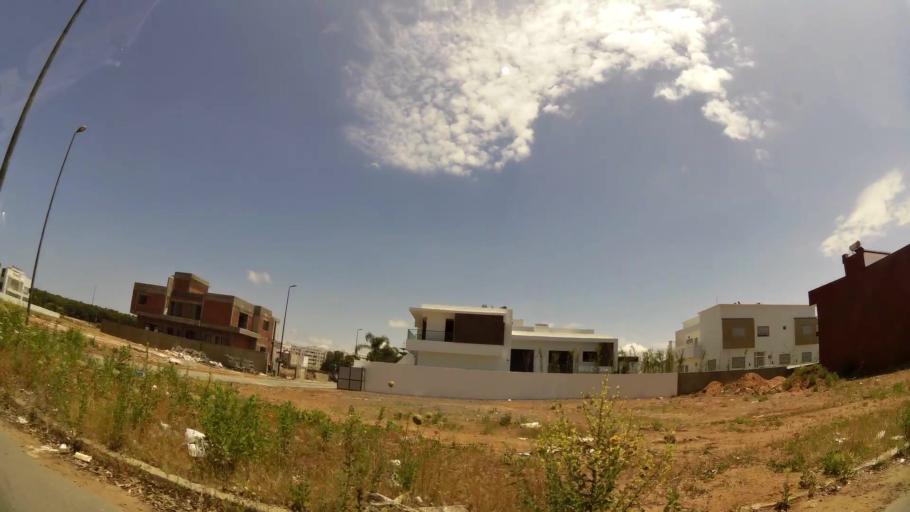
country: MA
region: Gharb-Chrarda-Beni Hssen
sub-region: Kenitra Province
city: Kenitra
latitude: 34.2688
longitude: -6.6321
